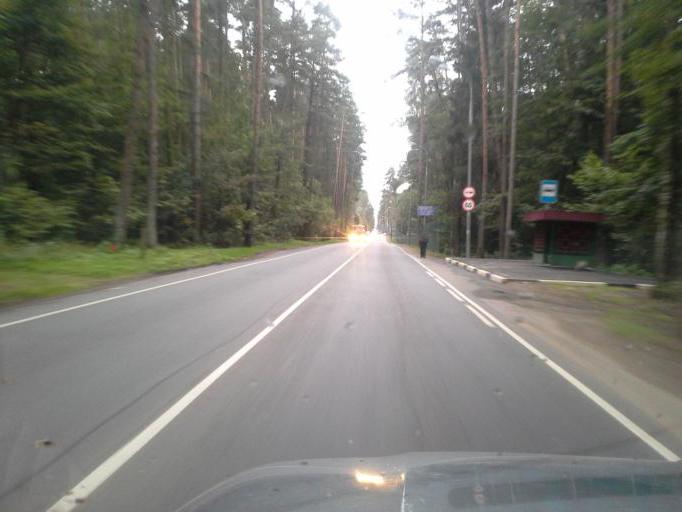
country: RU
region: Moskovskaya
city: Nikolina Gora
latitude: 55.7077
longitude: 37.0584
